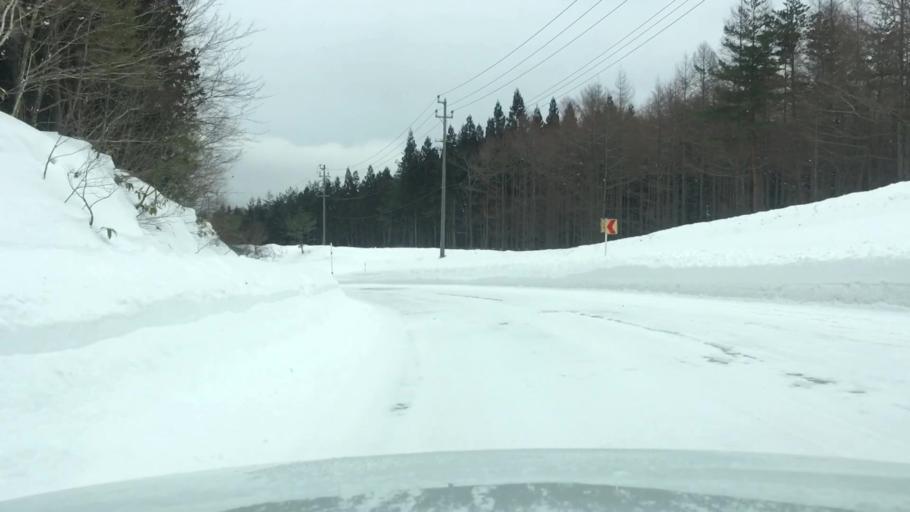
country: JP
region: Iwate
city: Shizukuishi
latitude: 39.9840
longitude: 141.0036
